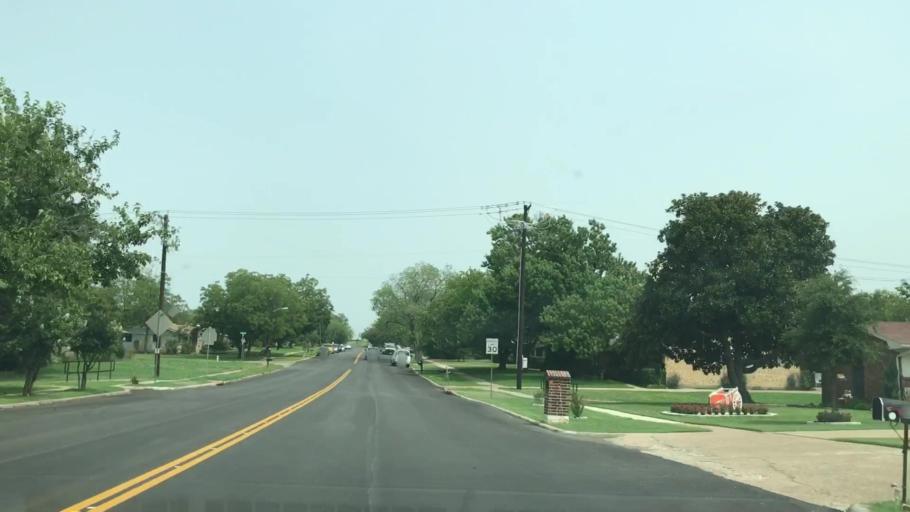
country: US
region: Texas
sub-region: Dallas County
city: Irving
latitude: 32.8475
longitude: -97.0005
